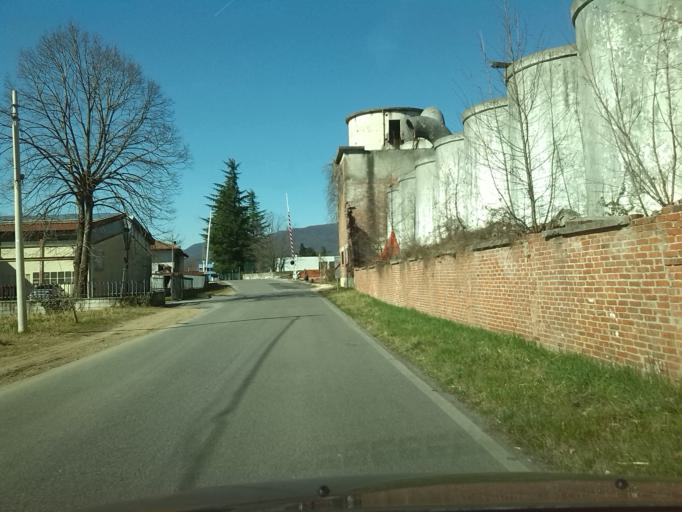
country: IT
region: Friuli Venezia Giulia
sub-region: Provincia di Udine
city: Cividale del Friuli
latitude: 46.0932
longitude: 13.4186
